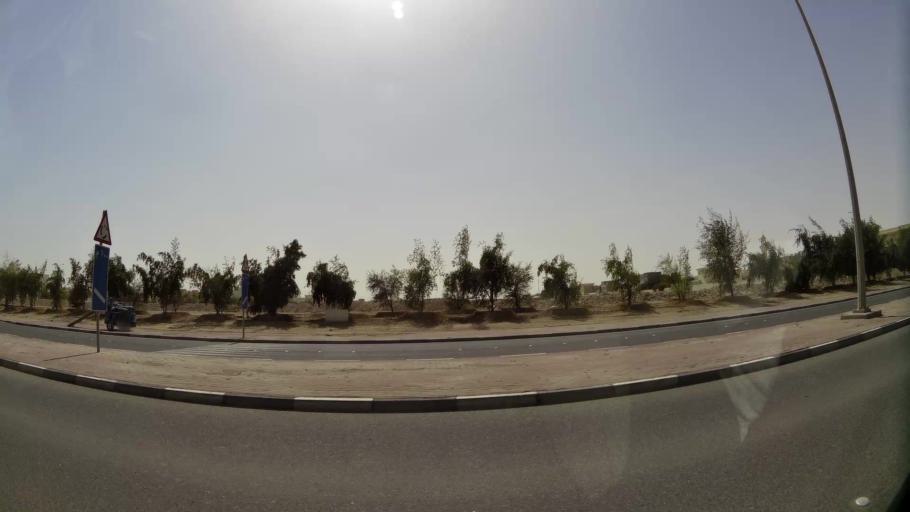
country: QA
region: Baladiyat Umm Salal
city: Umm Salal Muhammad
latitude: 25.3764
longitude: 51.4309
